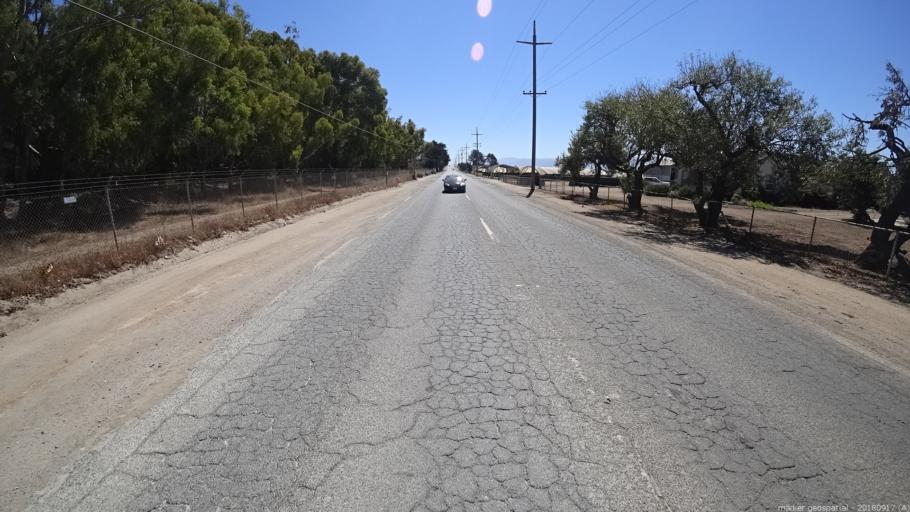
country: US
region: California
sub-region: Monterey County
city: Prunedale
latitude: 36.7521
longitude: -121.6083
